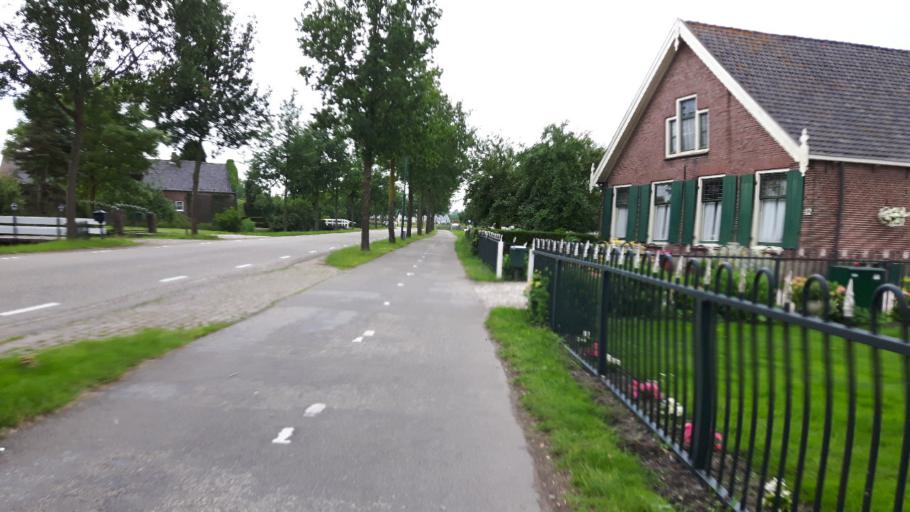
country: NL
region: Utrecht
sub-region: Stichtse Vecht
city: Spechtenkamp
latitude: 52.1163
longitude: 5.0091
